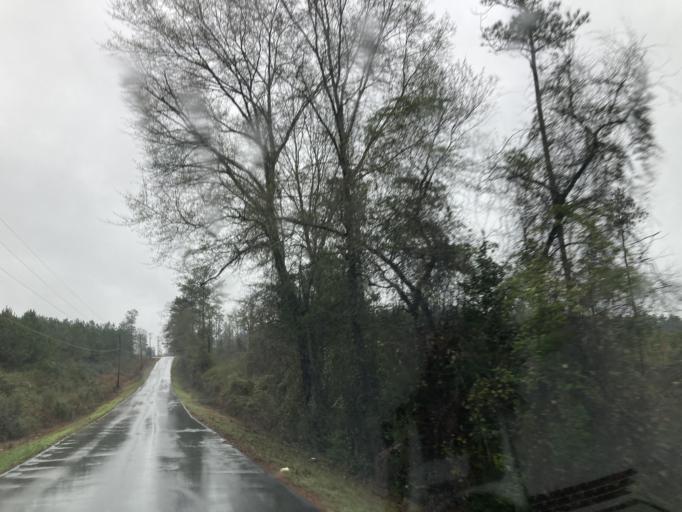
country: US
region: Mississippi
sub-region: Forrest County
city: Rawls Springs
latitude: 31.4787
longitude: -89.3823
